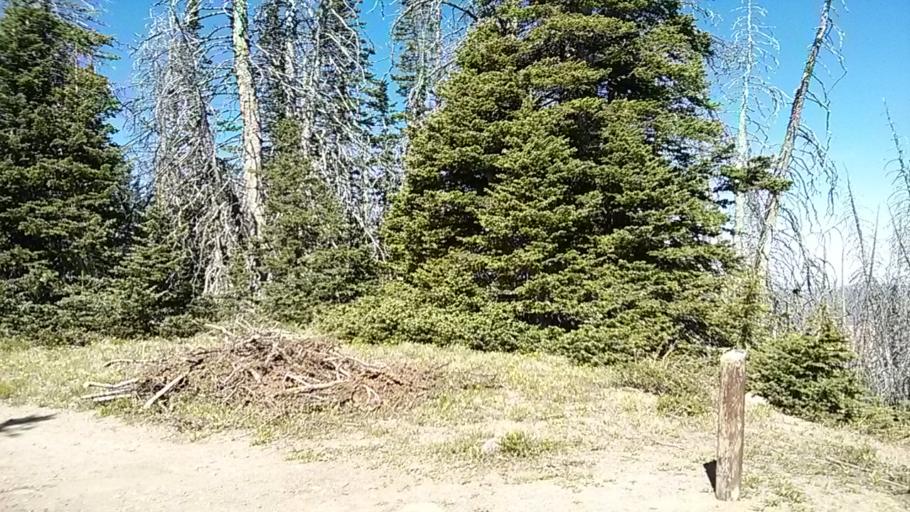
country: US
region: Utah
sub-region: Iron County
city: Parowan
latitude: 37.6353
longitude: -112.8241
